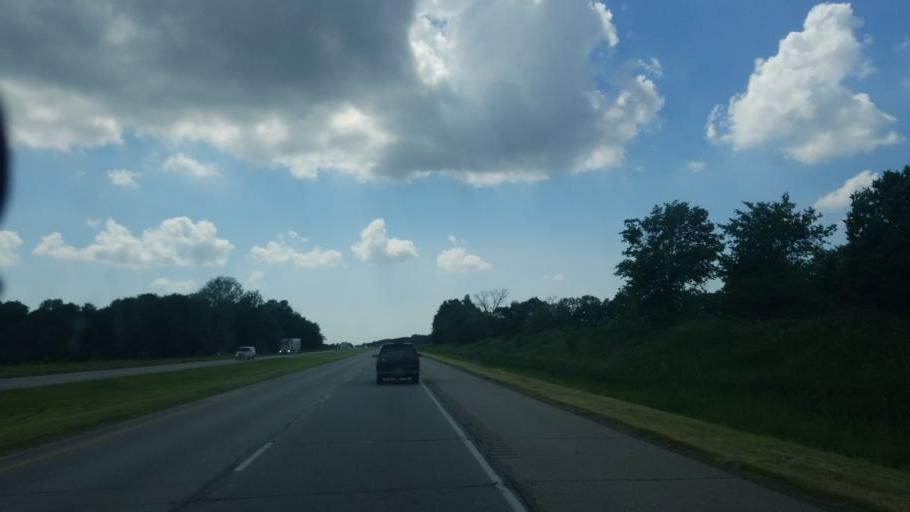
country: US
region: Indiana
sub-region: Kosciusko County
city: Warsaw
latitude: 41.2692
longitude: -85.9323
